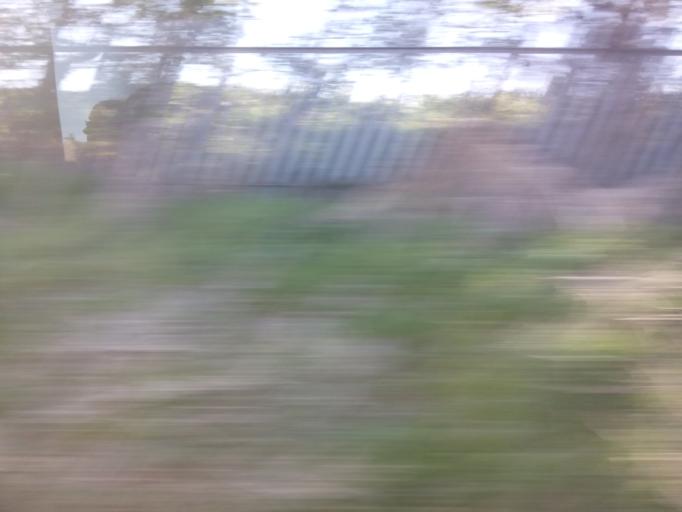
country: GB
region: Scotland
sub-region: East Lothian
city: Musselburgh
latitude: 55.9470
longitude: -3.0991
